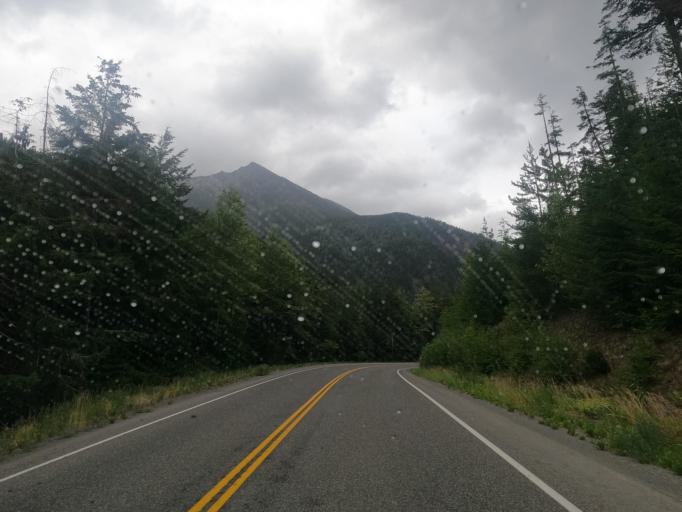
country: CA
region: British Columbia
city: Lillooet
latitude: 50.4868
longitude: -122.2057
